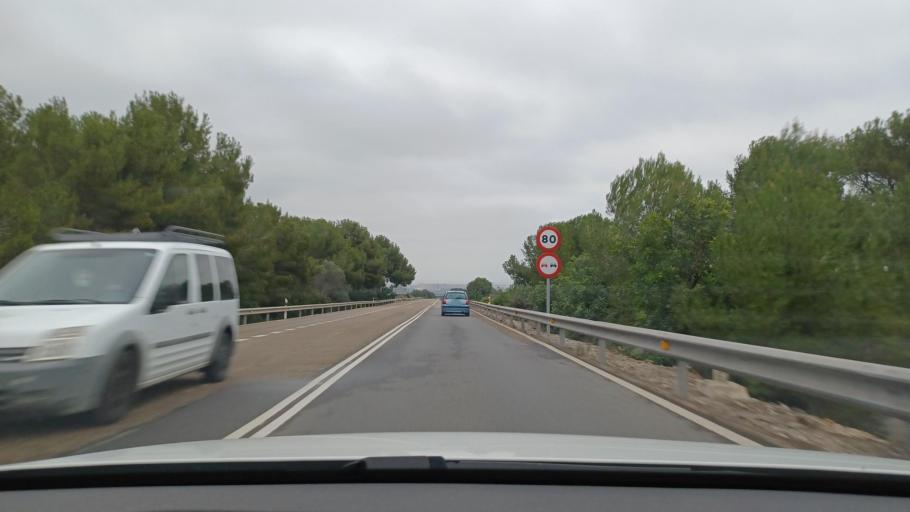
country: ES
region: Valencia
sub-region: Provincia de Castello
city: Orpesa/Oropesa del Mar
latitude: 40.0766
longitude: 0.1126
